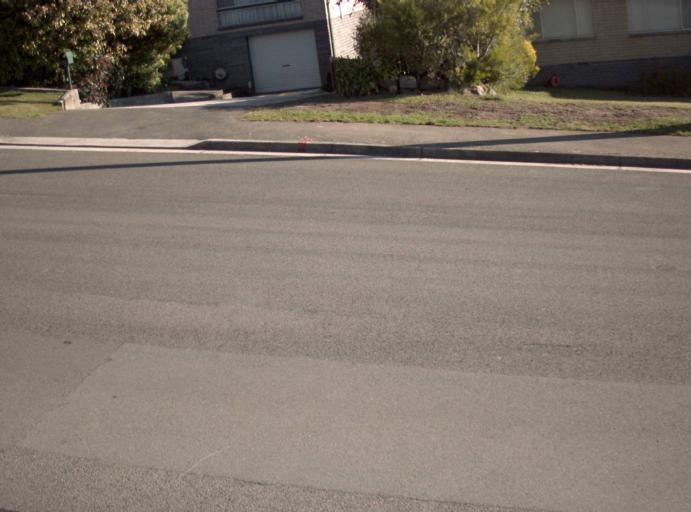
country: AU
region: Tasmania
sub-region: Launceston
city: Summerhill
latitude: -41.4650
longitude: 147.1216
